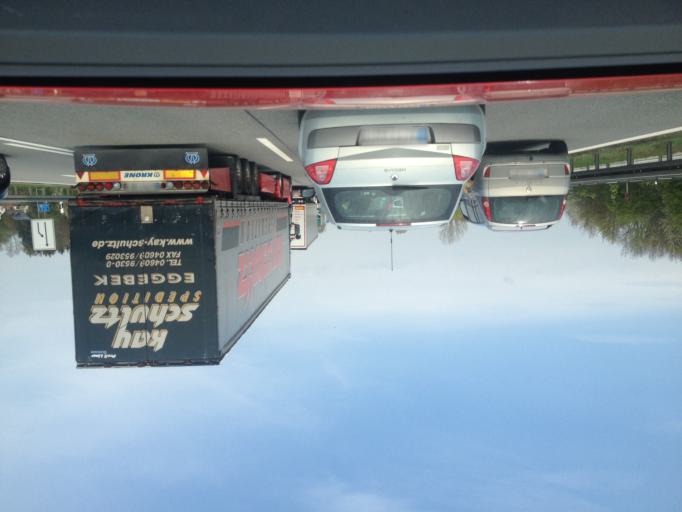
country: DE
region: Bavaria
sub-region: Upper Bavaria
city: Eching
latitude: 48.3255
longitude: 11.6159
